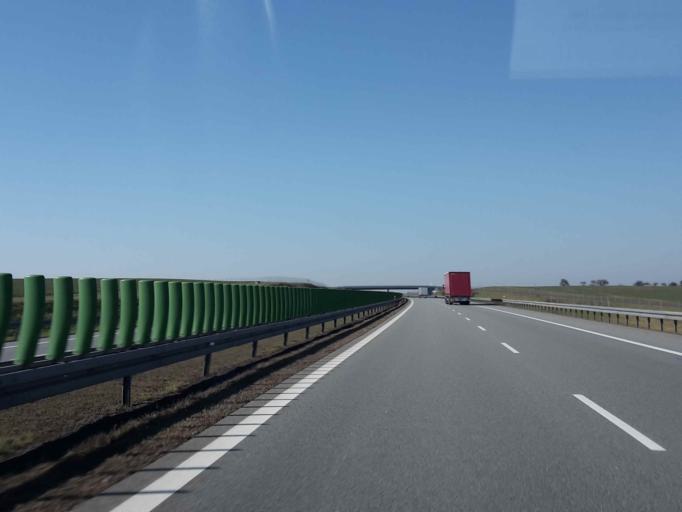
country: PL
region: Greater Poland Voivodeship
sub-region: Powiat nowotomyski
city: Kuslin
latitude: 52.3759
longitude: 16.2408
